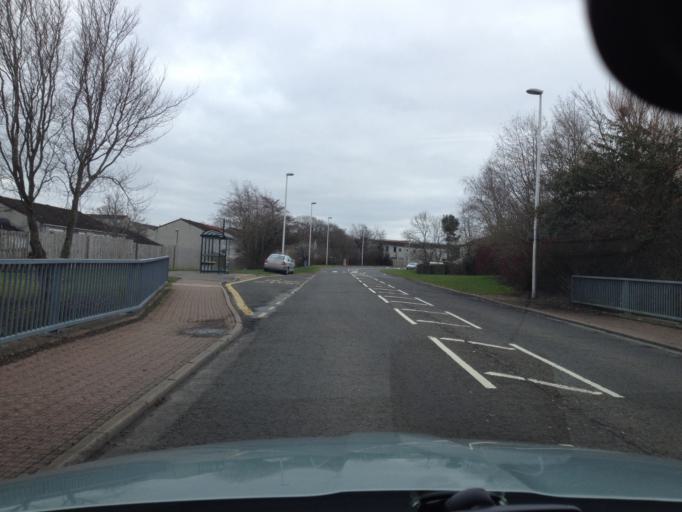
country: GB
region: Scotland
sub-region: West Lothian
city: Mid Calder
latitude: 55.8828
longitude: -3.4982
